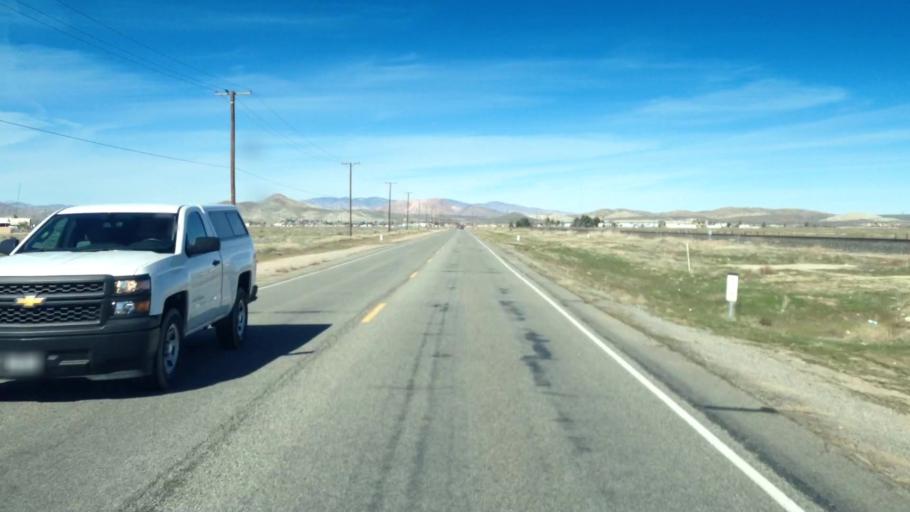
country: US
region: California
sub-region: Kern County
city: Rosamond
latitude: 34.8247
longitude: -118.1568
